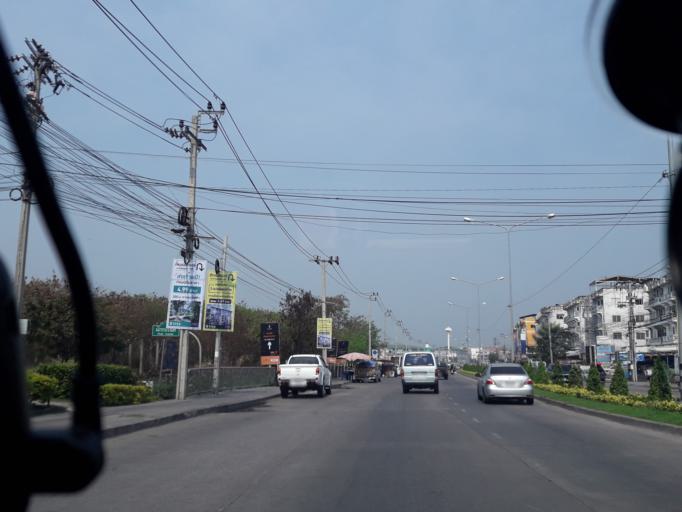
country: TH
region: Bangkok
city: Khan Na Yao
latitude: 13.8361
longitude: 100.6971
